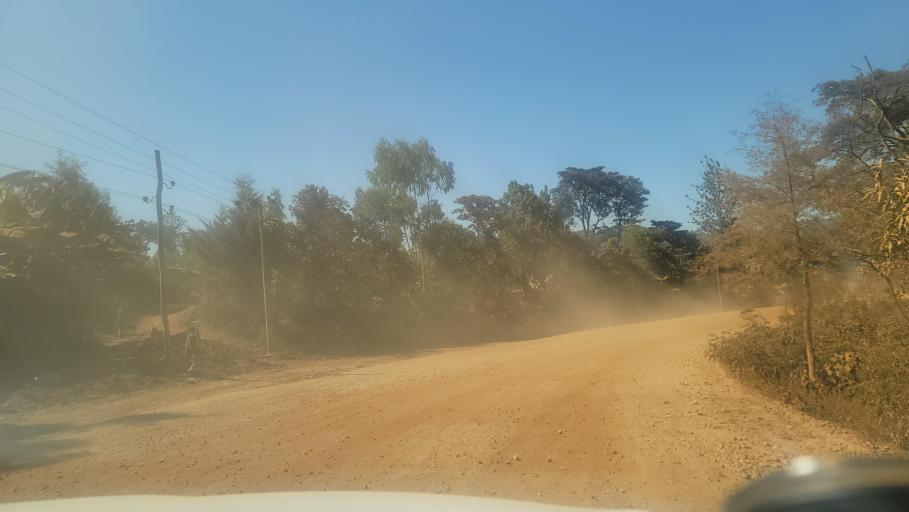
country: ET
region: Oromiya
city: Agaro
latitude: 7.8372
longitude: 36.5539
